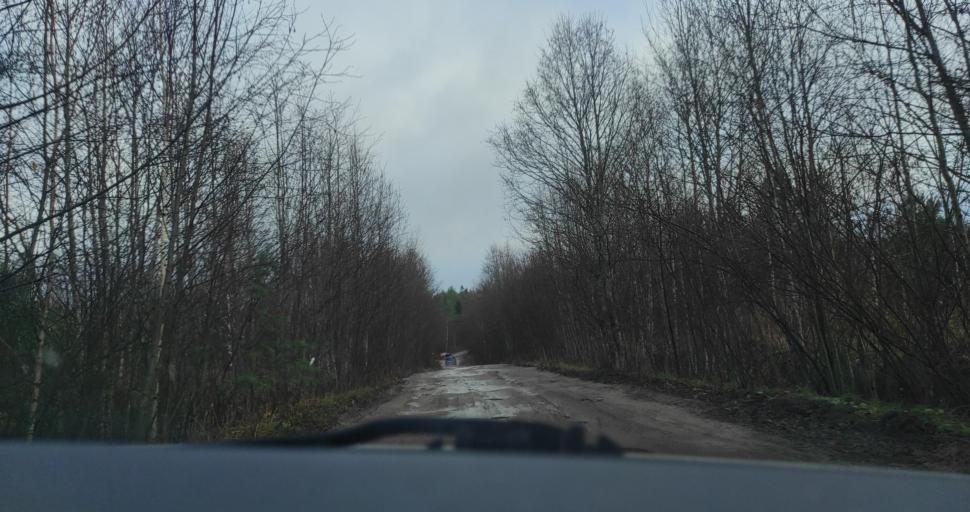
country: RU
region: Republic of Karelia
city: Pitkyaranta
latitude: 61.7346
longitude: 31.3864
